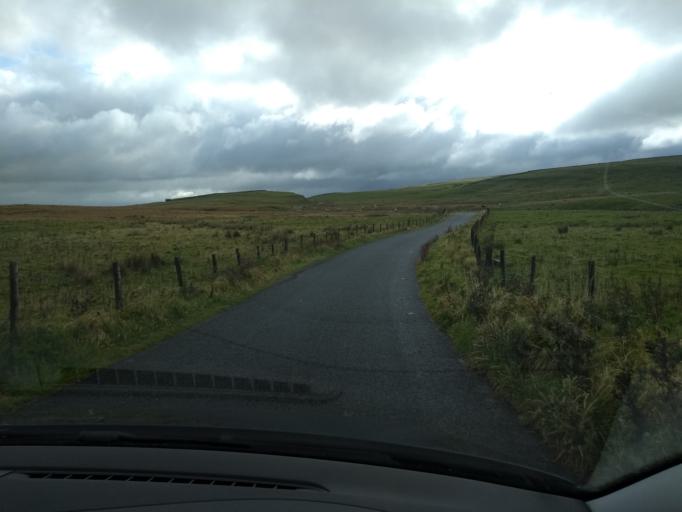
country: GB
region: England
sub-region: North Yorkshire
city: Settle
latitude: 54.0920
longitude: -2.1855
